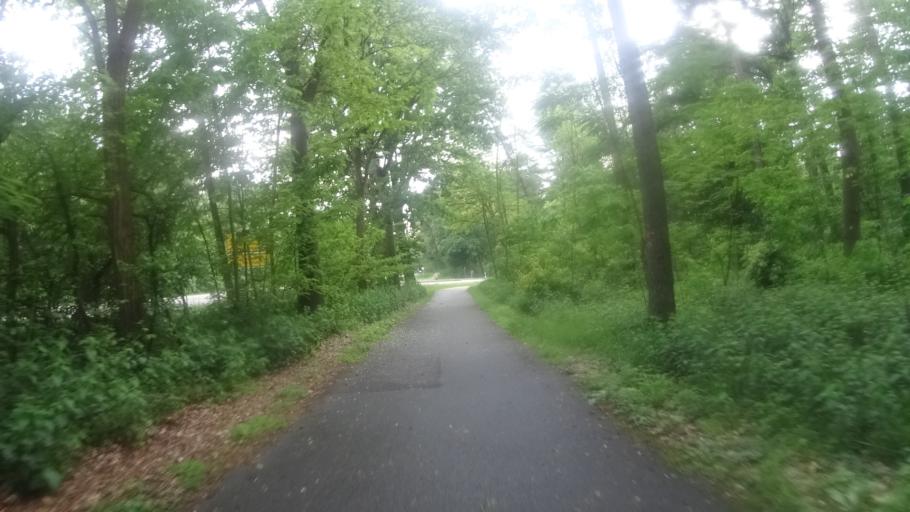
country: DE
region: Baden-Wuerttemberg
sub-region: Karlsruhe Region
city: Rastatt
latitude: 48.8357
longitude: 8.1827
